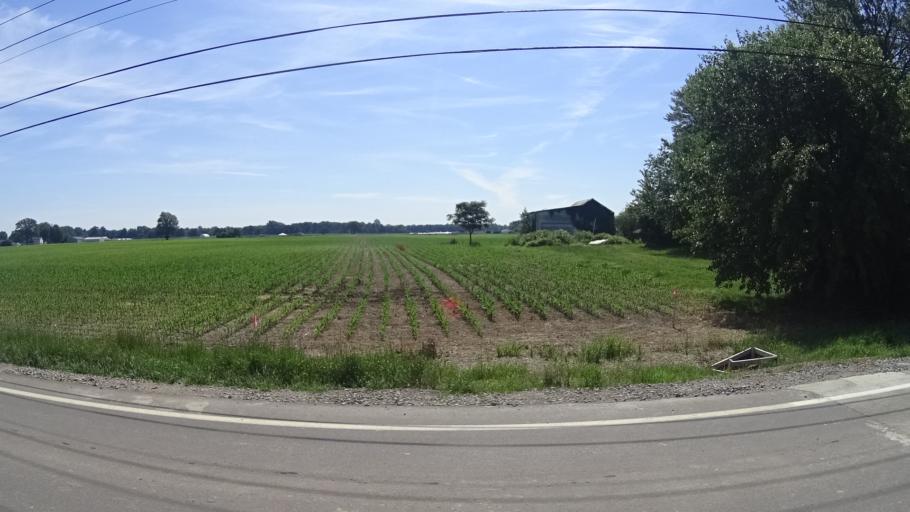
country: US
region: Ohio
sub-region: Erie County
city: Huron
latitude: 41.3749
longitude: -82.4929
